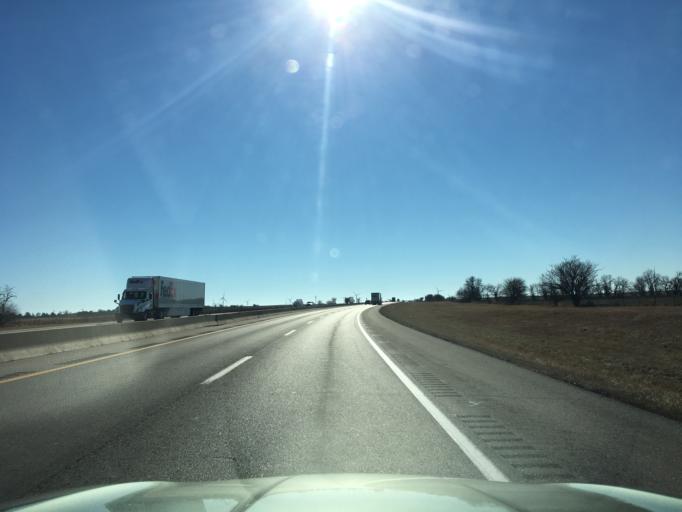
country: US
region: Kansas
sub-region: Sumner County
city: Wellington
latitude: 37.1840
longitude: -97.3398
